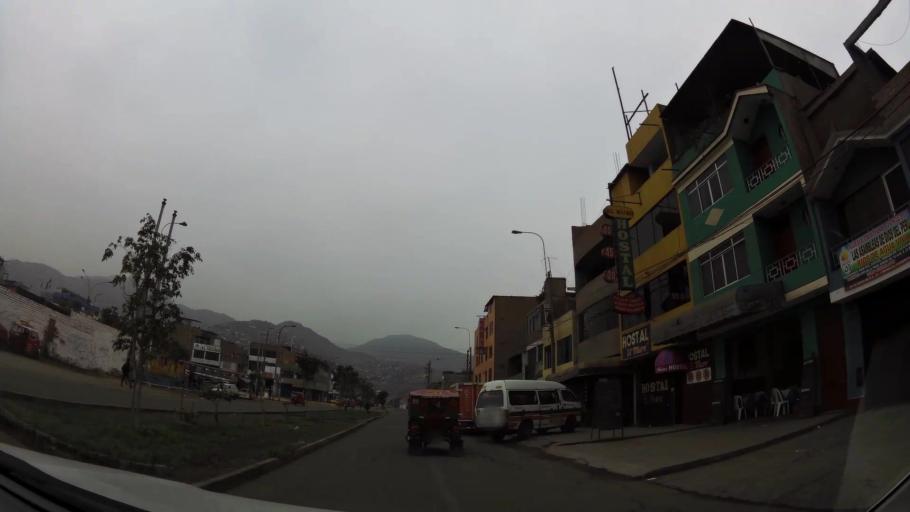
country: PE
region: Lima
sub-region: Lima
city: Independencia
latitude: -11.9500
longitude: -76.9815
